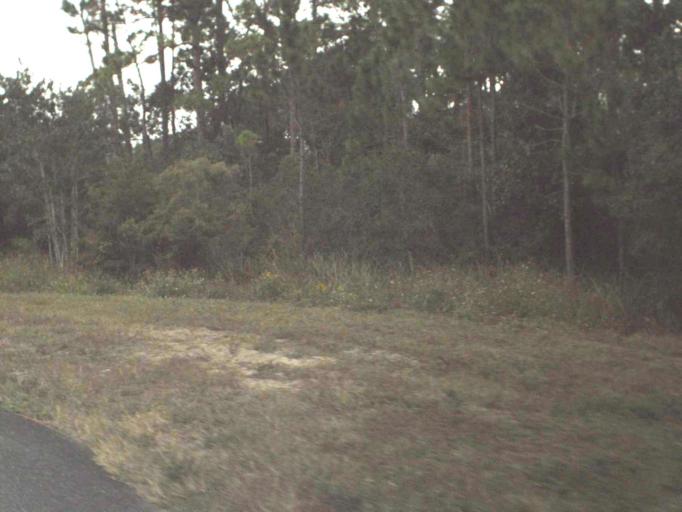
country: US
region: Florida
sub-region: Wakulla County
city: Crawfordville
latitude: 29.9960
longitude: -84.3977
